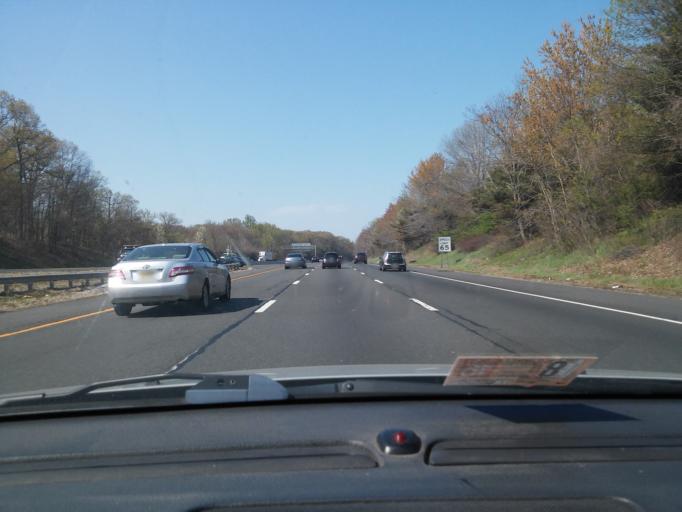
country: US
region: New Jersey
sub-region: Union County
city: Springfield
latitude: 40.7053
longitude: -74.3419
